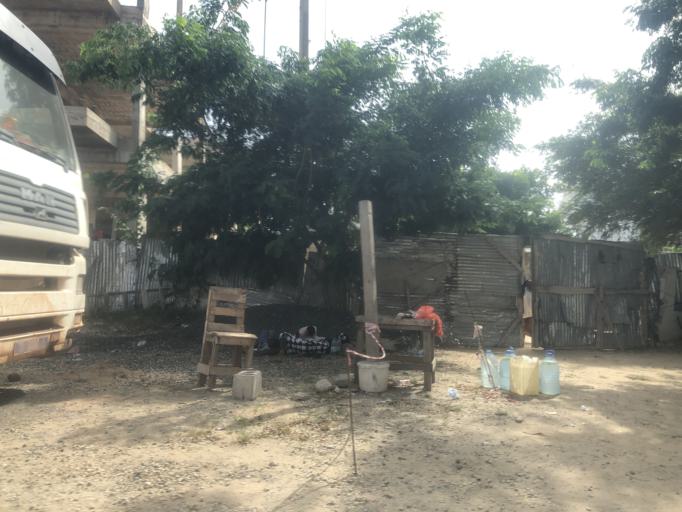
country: SN
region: Dakar
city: Mermoz Boabab
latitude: 14.7386
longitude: -17.5133
